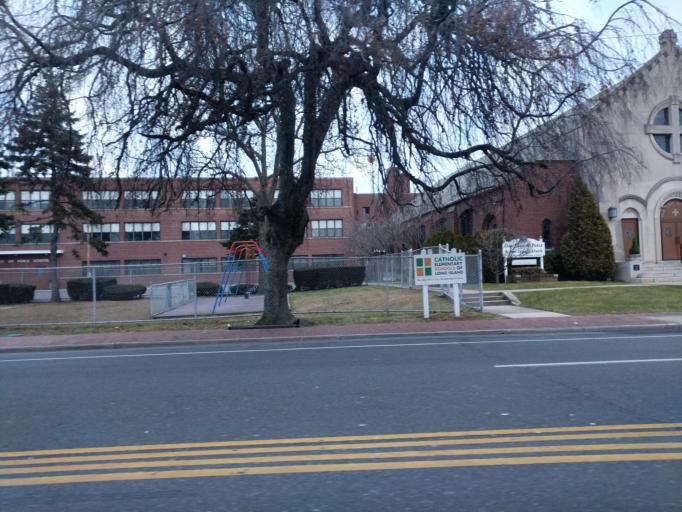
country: US
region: New York
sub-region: Nassau County
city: Lynbrook
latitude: 40.6583
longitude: -73.6759
